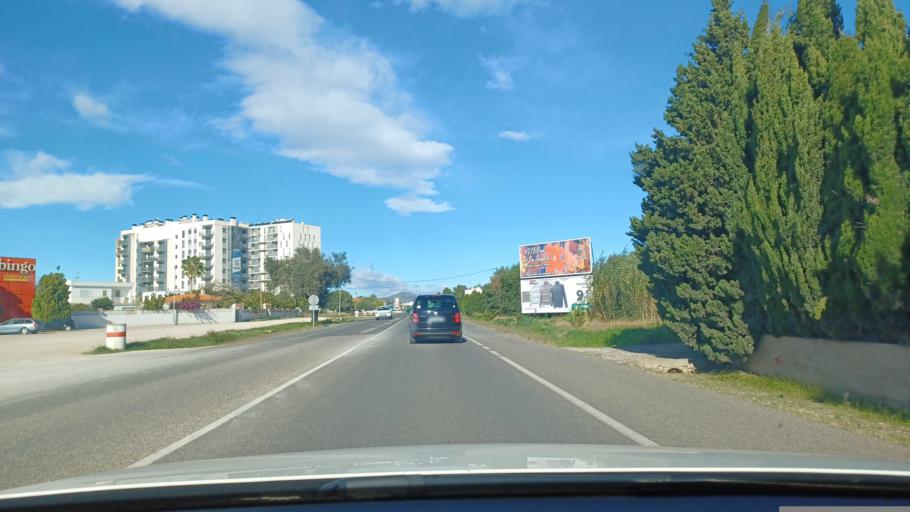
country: ES
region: Valencia
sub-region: Provincia de Castello
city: Vinaros
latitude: 40.4651
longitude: 0.4641
